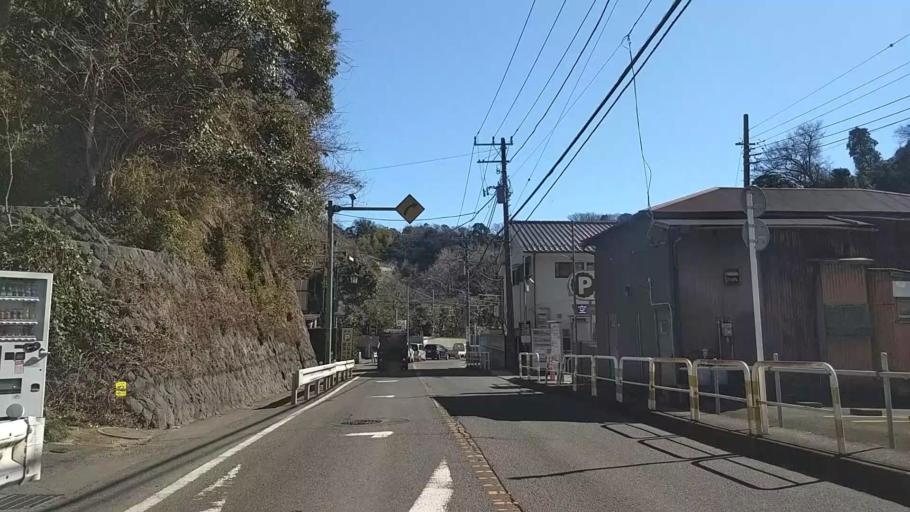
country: JP
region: Kanagawa
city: Kamakura
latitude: 35.3169
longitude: 139.5343
